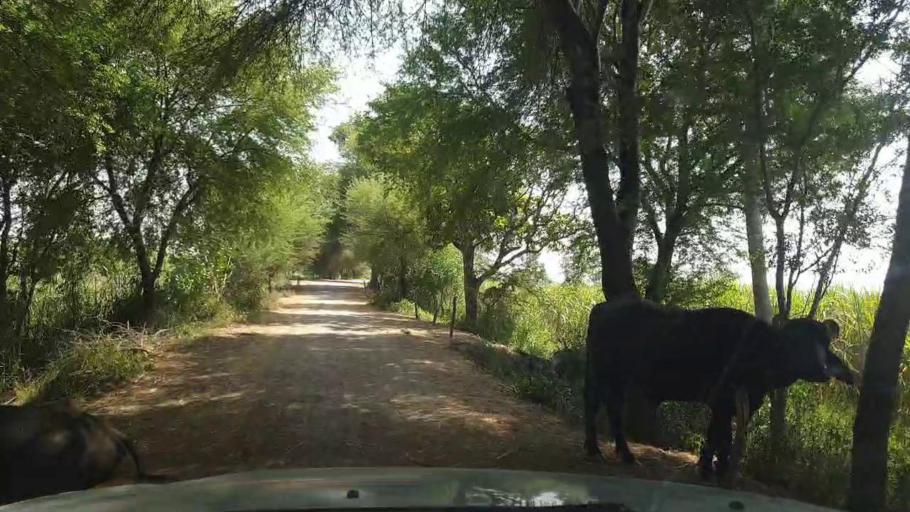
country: PK
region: Sindh
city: Bulri
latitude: 24.8800
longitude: 68.4044
